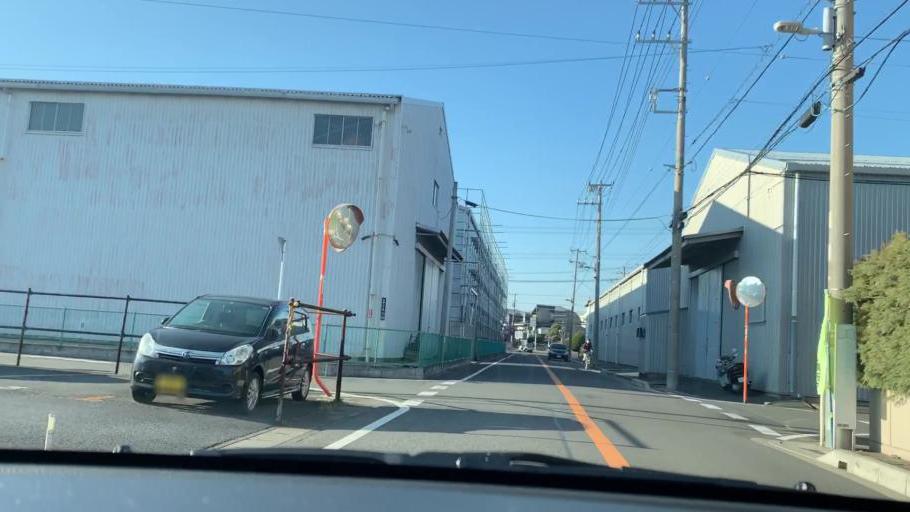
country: JP
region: Tokyo
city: Urayasu
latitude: 35.6509
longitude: 139.8961
